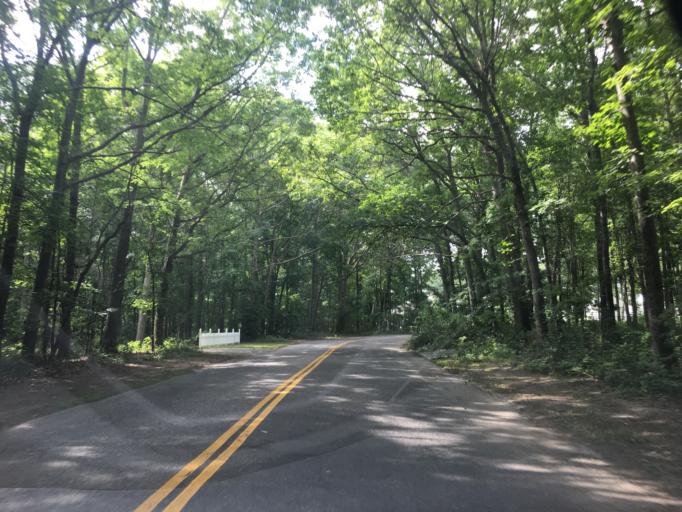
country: US
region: New York
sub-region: Suffolk County
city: Shelter Island Heights
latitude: 41.0968
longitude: -72.3315
